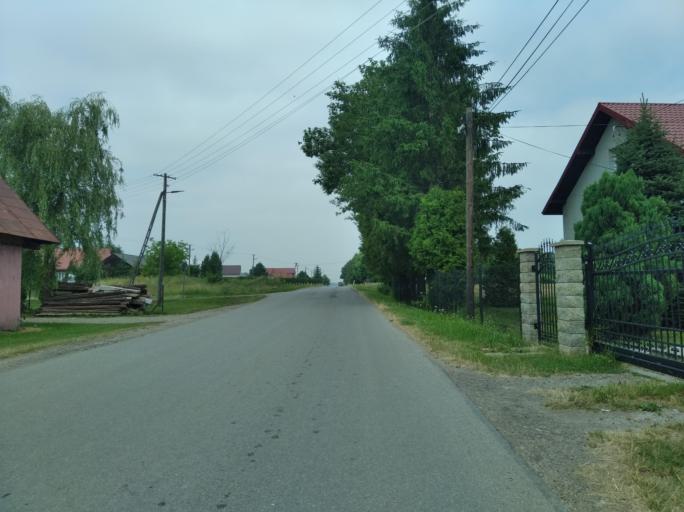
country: PL
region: Subcarpathian Voivodeship
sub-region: Powiat sanocki
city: Besko
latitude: 49.5963
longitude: 21.9616
